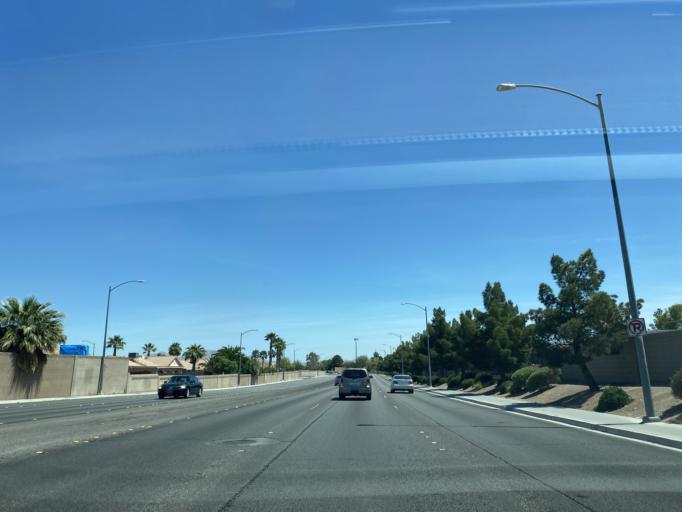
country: US
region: Nevada
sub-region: Clark County
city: Las Vegas
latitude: 36.1971
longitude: -115.1751
